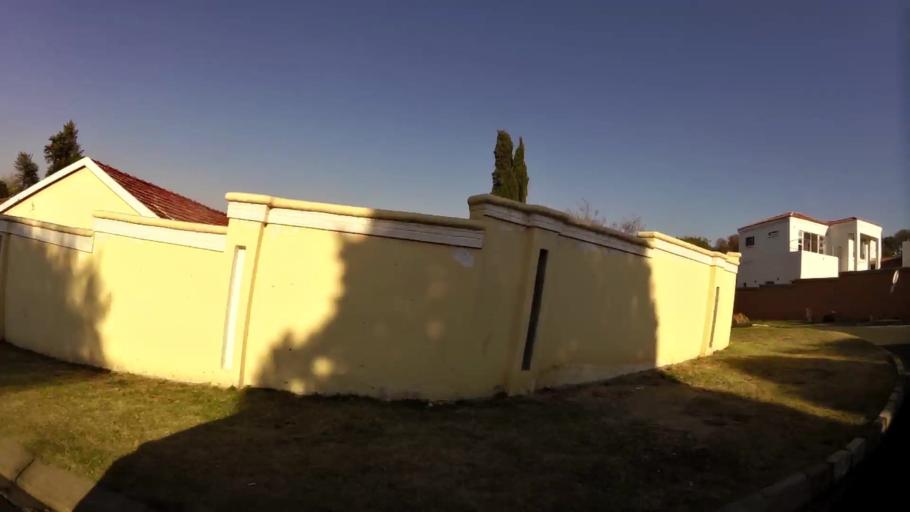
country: ZA
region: Gauteng
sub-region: City of Johannesburg Metropolitan Municipality
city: Soweto
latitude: -26.2793
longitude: 27.9588
